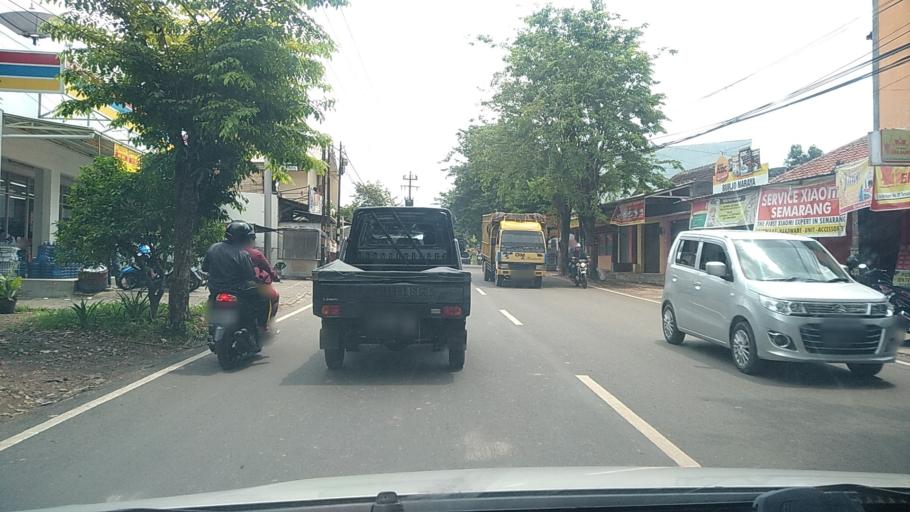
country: ID
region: Central Java
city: Semarang
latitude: -7.0594
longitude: 110.4381
